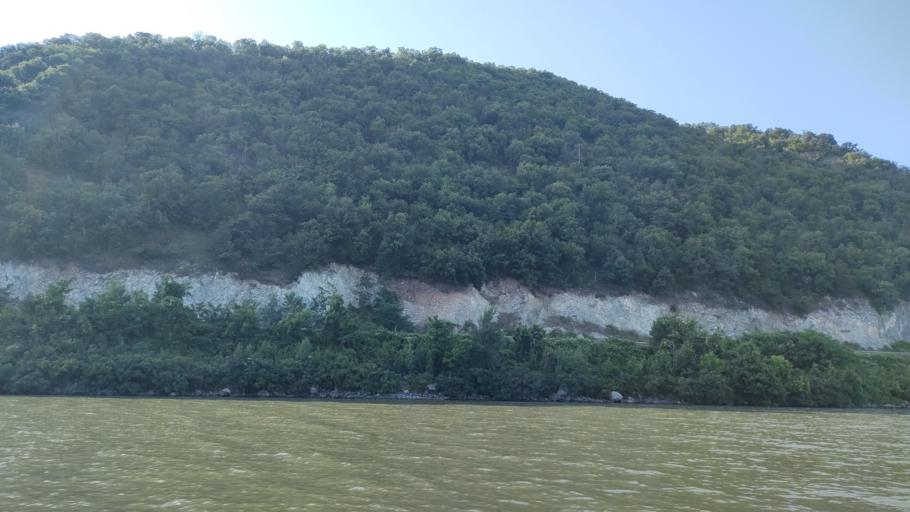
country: RO
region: Mehedinti
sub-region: Comuna Svinita
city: Svinita
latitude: 44.4815
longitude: 22.1752
